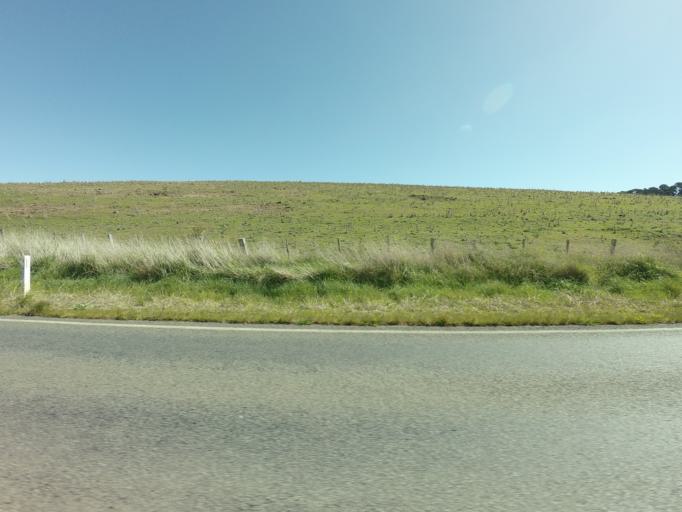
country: AU
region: Tasmania
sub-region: Derwent Valley
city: New Norfolk
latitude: -42.6362
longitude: 146.9169
